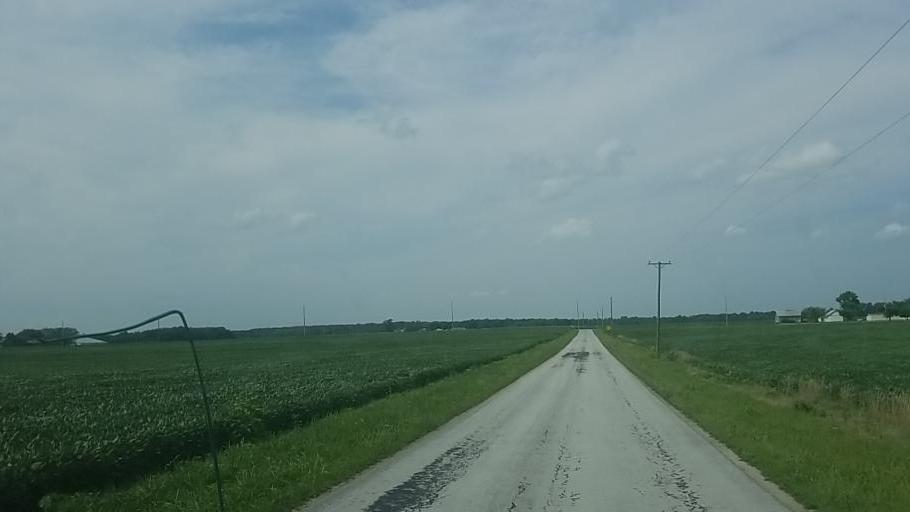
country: US
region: Ohio
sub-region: Hardin County
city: Forest
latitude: 40.7787
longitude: -83.5572
